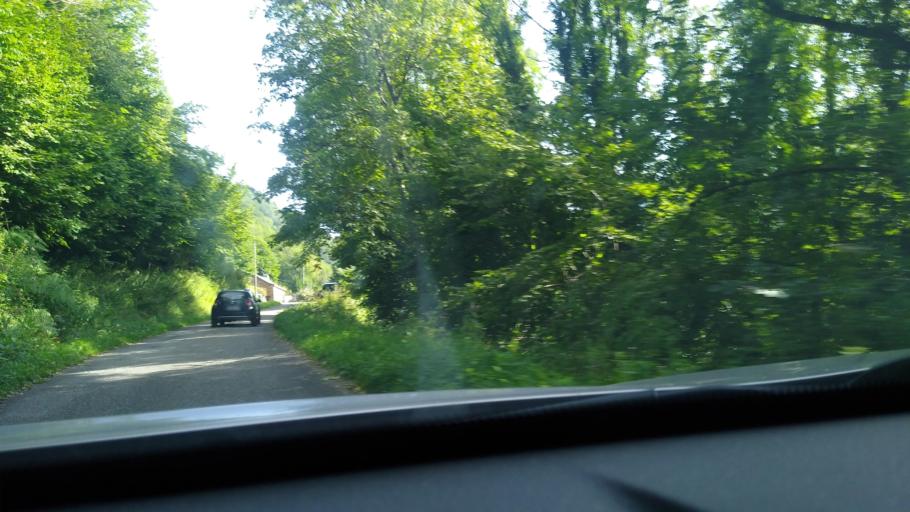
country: FR
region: Midi-Pyrenees
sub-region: Departement de l'Ariege
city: Saint-Girons
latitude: 42.7965
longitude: 1.1870
